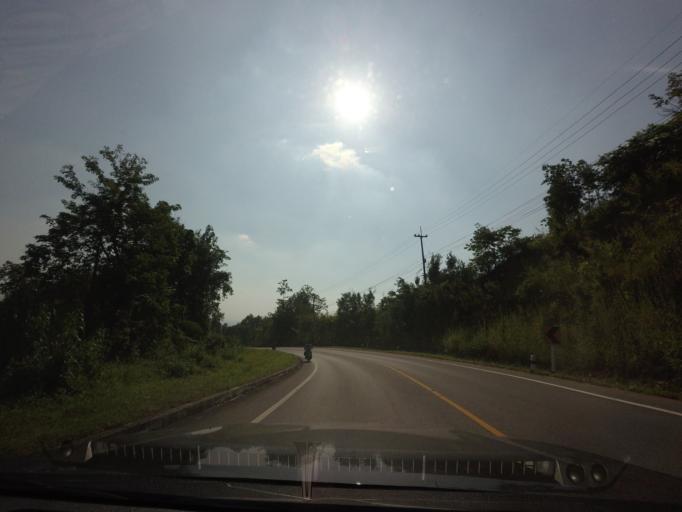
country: TH
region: Nan
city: Santi Suk
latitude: 18.9077
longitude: 100.8594
